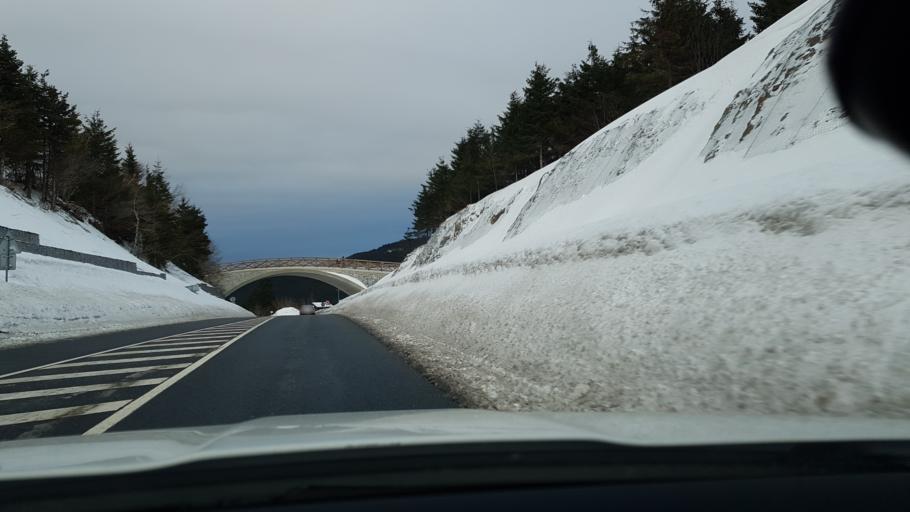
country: CZ
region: Olomoucky
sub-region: Okres Sumperk
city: Loucna nad Desnou
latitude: 50.1242
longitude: 17.1530
